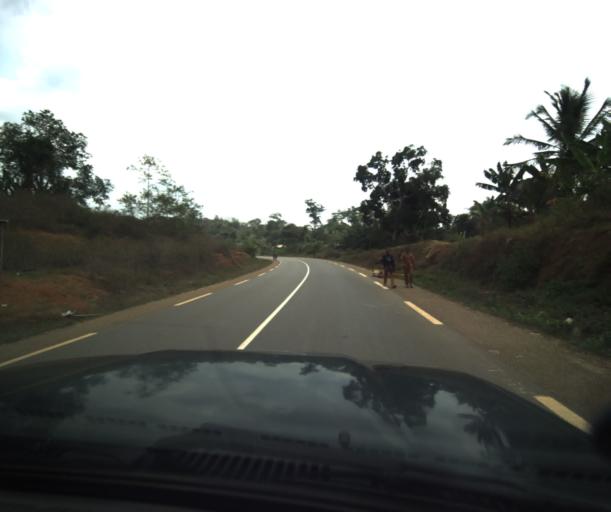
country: CM
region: Centre
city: Akono
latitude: 3.5600
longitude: 11.3034
